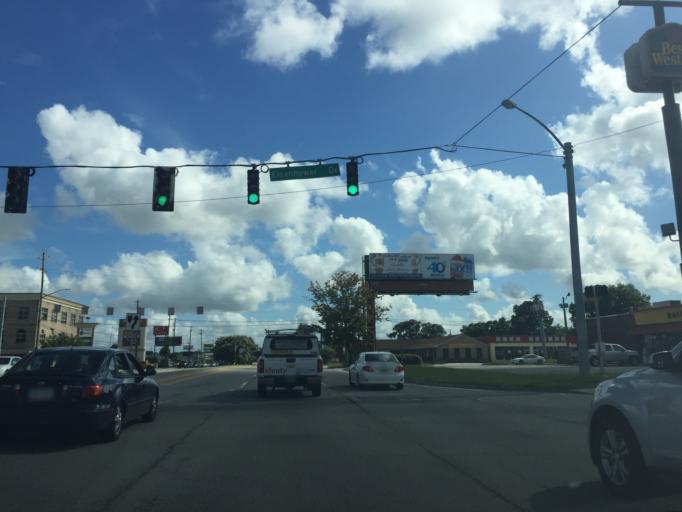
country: US
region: Georgia
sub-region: Chatham County
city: Isle of Hope
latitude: 32.0102
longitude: -81.1146
